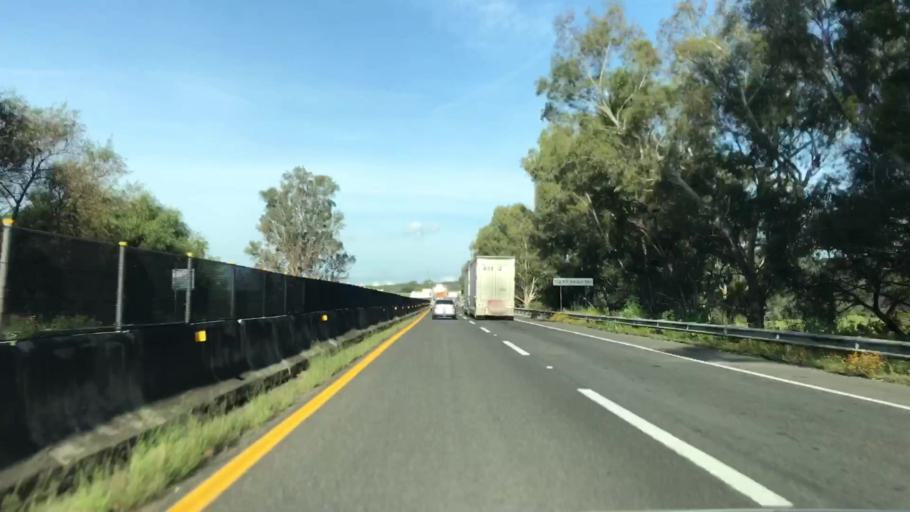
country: MX
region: Jalisco
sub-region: Lagos de Moreno
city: Cristeros [Fraccionamiento]
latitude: 21.3178
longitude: -102.0500
